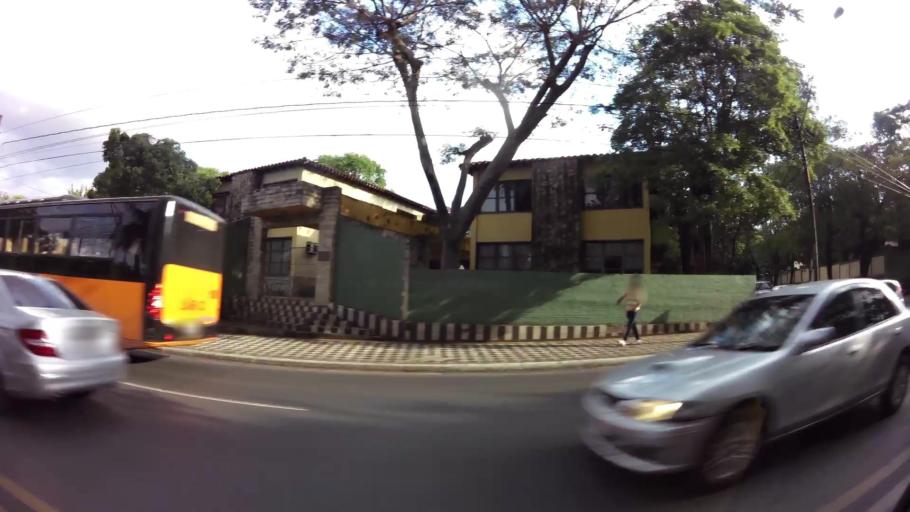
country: PY
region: Asuncion
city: Asuncion
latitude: -25.2936
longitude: -57.6095
